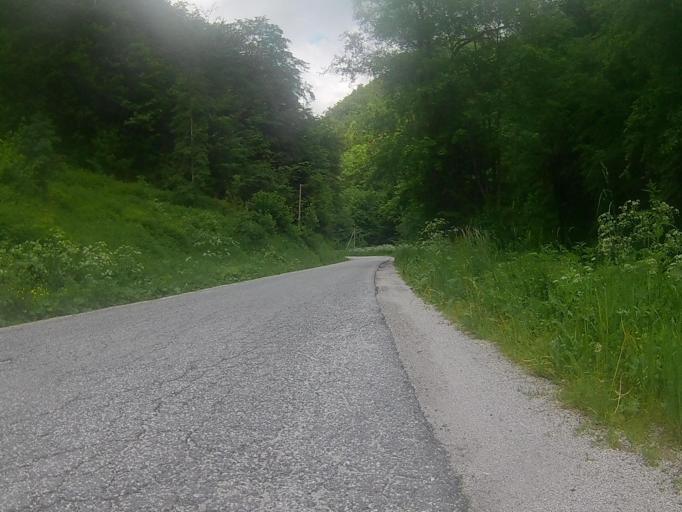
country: SI
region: Maribor
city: Bresternica
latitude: 46.5980
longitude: 15.5550
